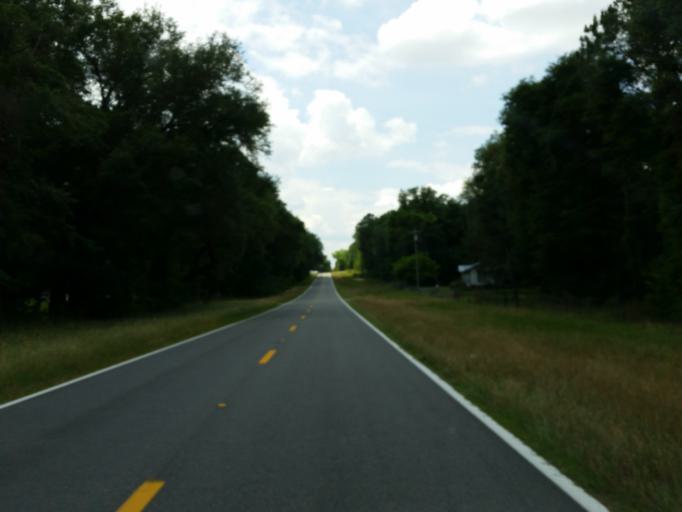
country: US
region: Florida
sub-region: Alachua County
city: High Springs
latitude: 29.9524
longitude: -82.5993
